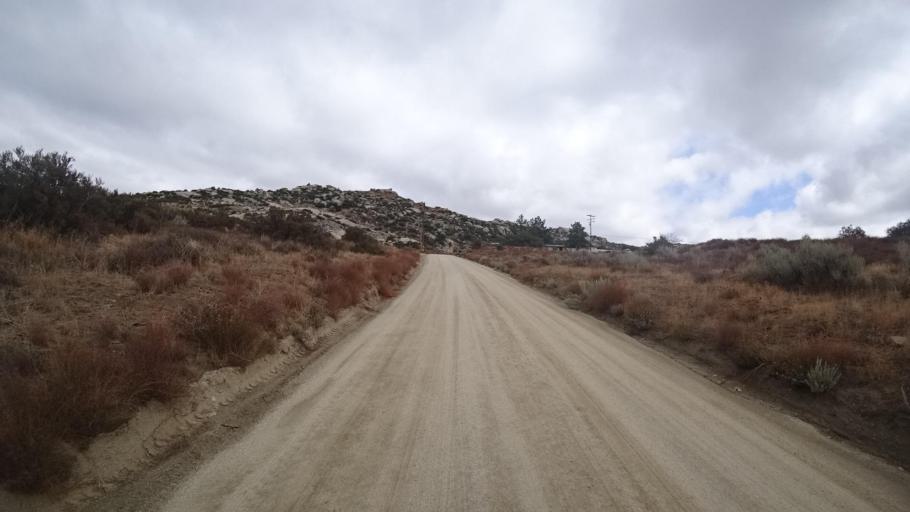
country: US
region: California
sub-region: San Diego County
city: Campo
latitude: 32.7090
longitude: -116.3872
